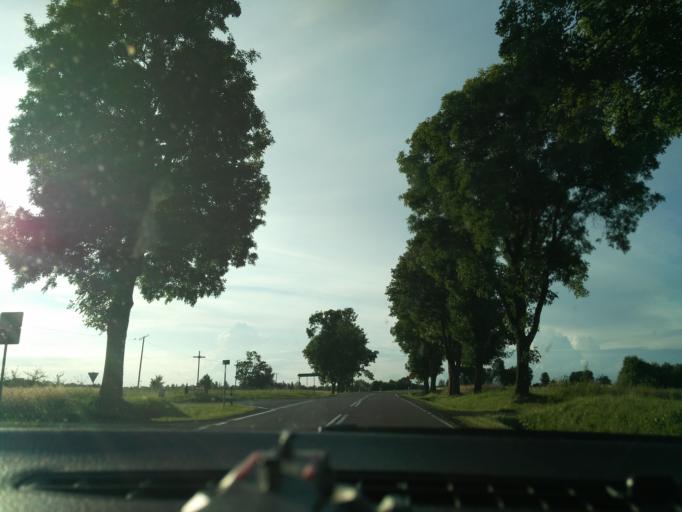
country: PL
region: Lublin Voivodeship
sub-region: Powiat krasnicki
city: Krasnik
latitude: 50.8802
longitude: 22.2626
